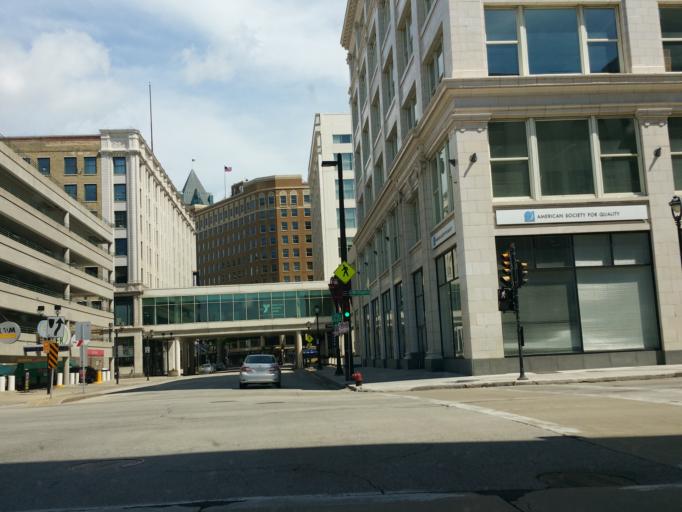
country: US
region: Wisconsin
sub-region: Milwaukee County
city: Milwaukee
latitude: 43.0374
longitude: -87.9111
